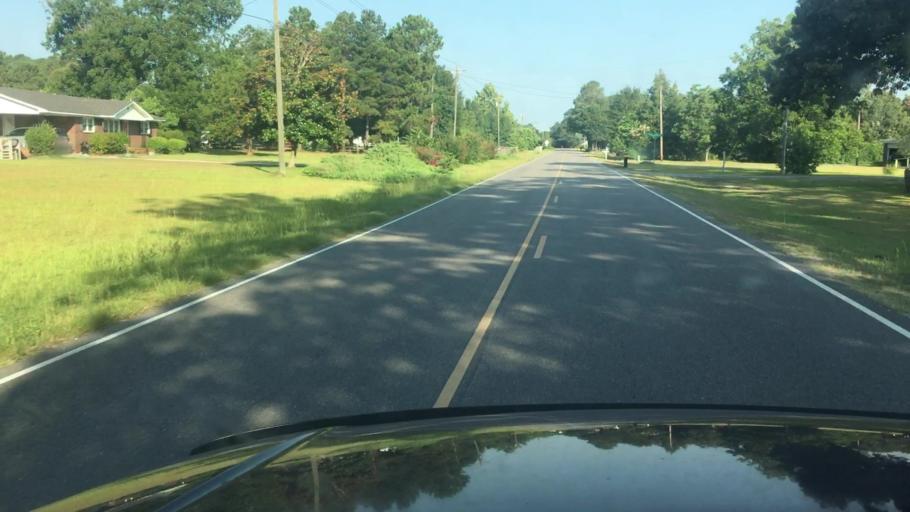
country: US
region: North Carolina
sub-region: Robeson County
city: Saint Pauls
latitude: 34.8483
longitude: -78.8603
